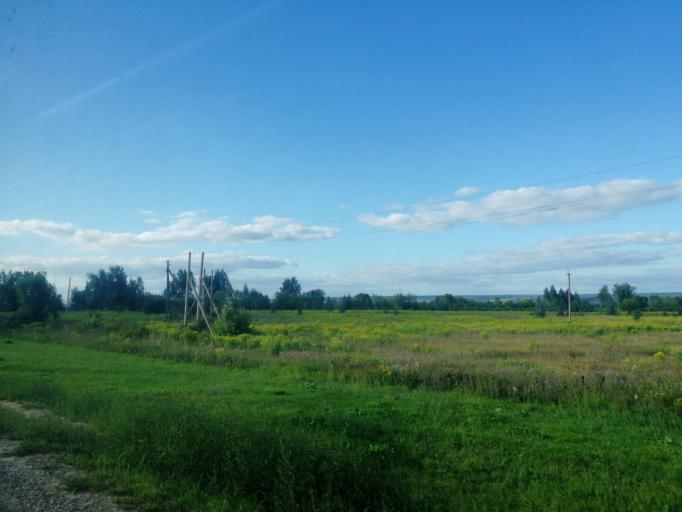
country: RU
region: Tula
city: Leninskiy
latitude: 54.2461
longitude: 37.3259
